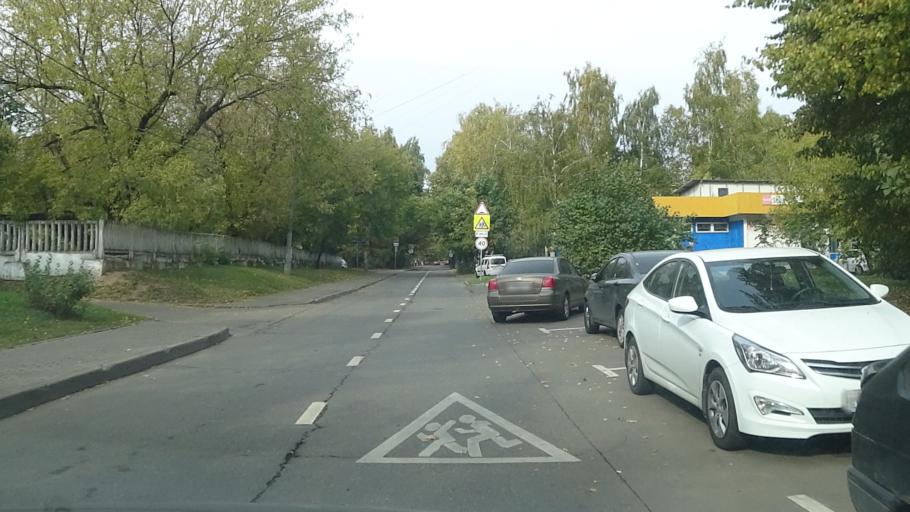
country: RU
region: Moscow
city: Solntsevo
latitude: 55.6565
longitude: 37.3912
